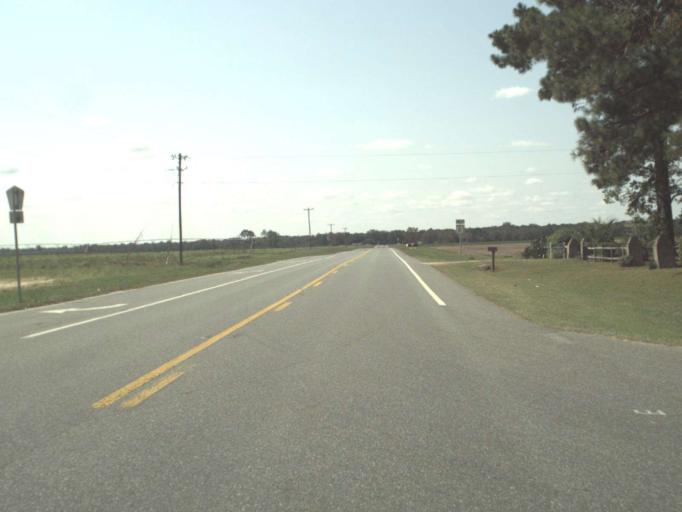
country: US
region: Florida
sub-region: Jackson County
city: Malone
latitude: 30.9519
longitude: -85.2397
